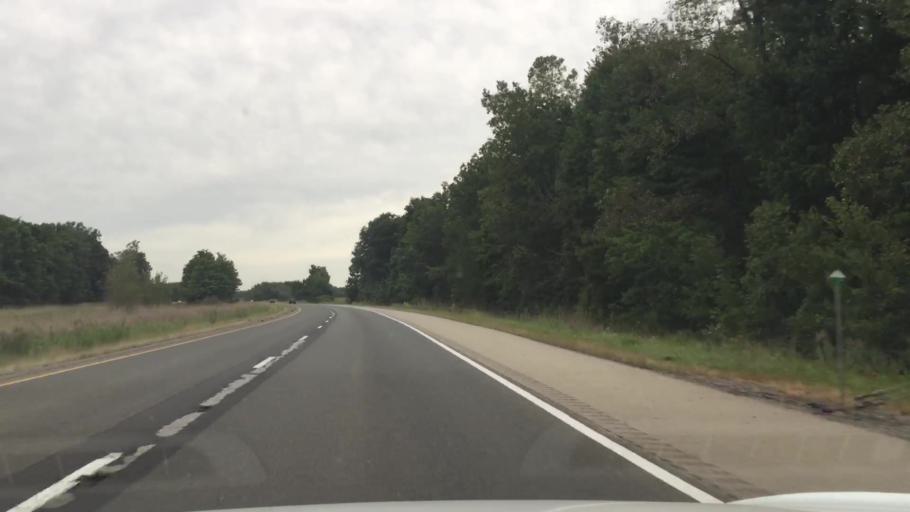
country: CA
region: Ontario
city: Lambton Shores
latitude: 42.9922
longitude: -81.9329
